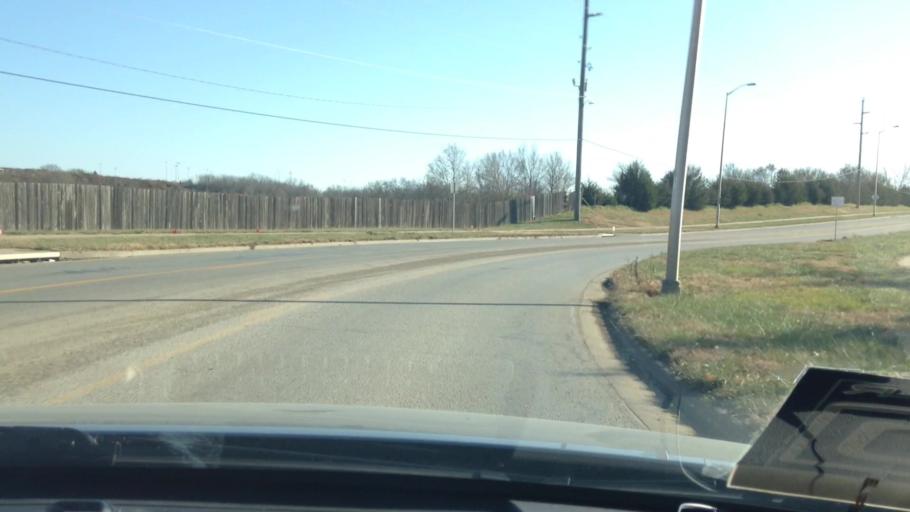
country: US
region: Kansas
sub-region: Johnson County
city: Olathe
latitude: 38.8978
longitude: -94.8533
